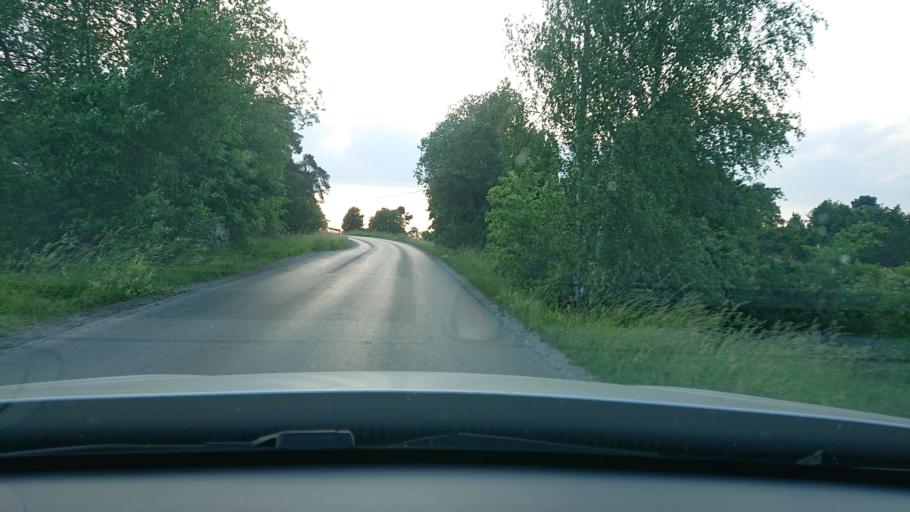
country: SE
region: Stockholm
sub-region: Osterakers Kommun
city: Akersberga
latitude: 59.5081
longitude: 18.3156
